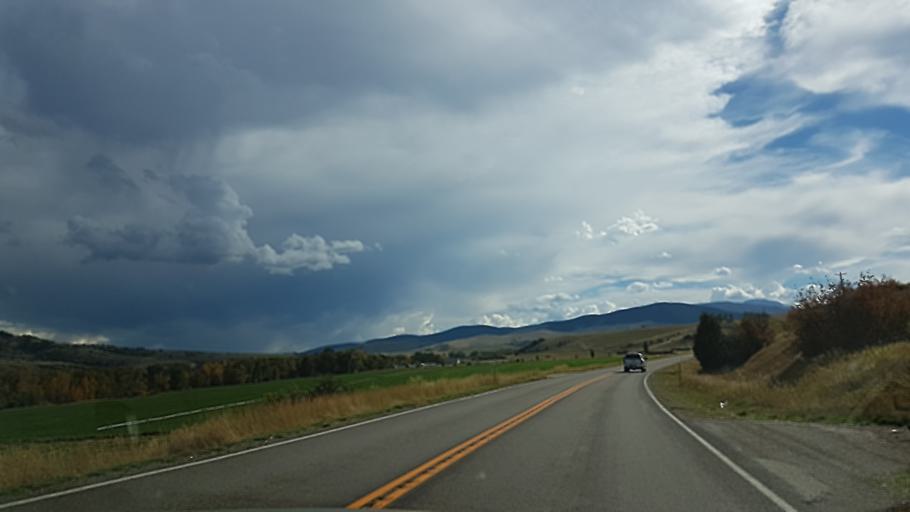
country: US
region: Montana
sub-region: Jefferson County
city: Whitehall
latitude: 45.8207
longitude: -111.9330
